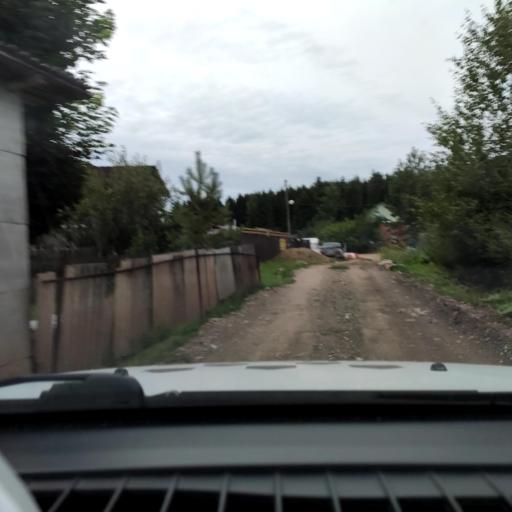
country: RU
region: Perm
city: Froly
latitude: 57.9351
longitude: 56.2530
